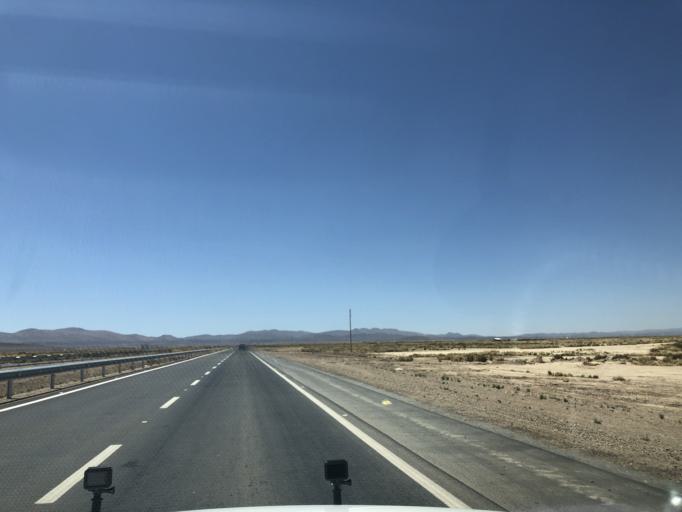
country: BO
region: La Paz
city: Colquiri
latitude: -17.6494
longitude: -67.1990
